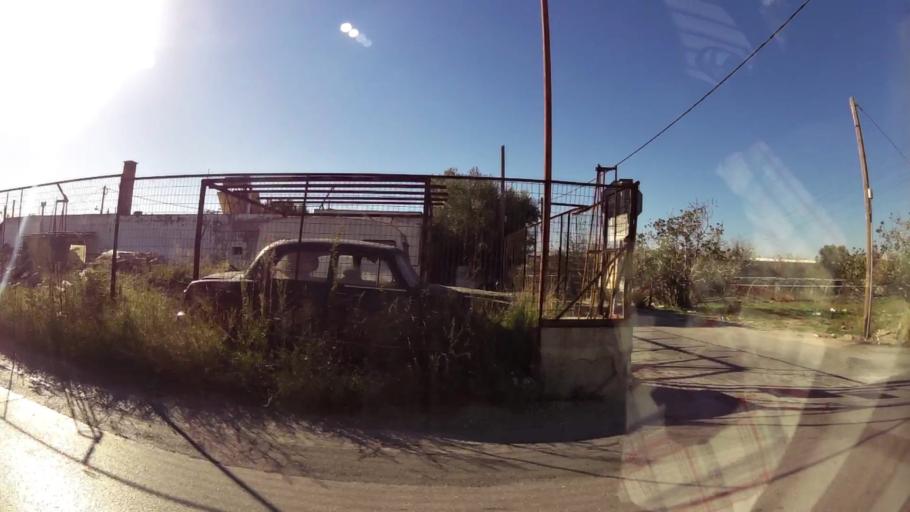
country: GR
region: Attica
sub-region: Nomarchia Anatolikis Attikis
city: Acharnes
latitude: 38.0796
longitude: 23.7513
